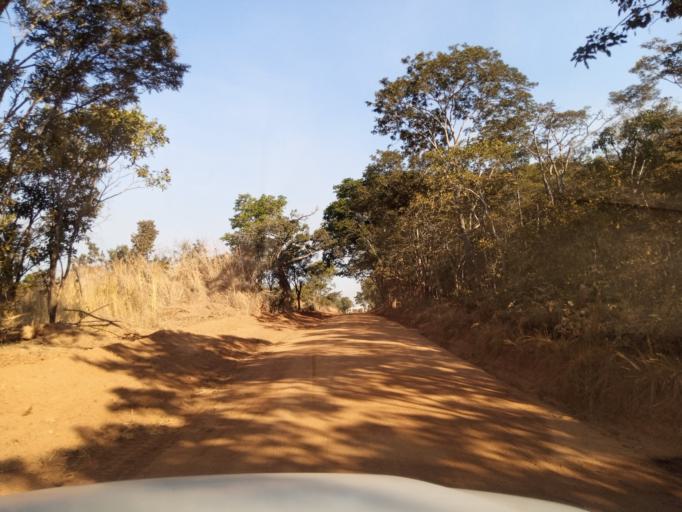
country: CD
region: Katanga
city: Lubumbashi
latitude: -11.3058
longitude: 27.2835
